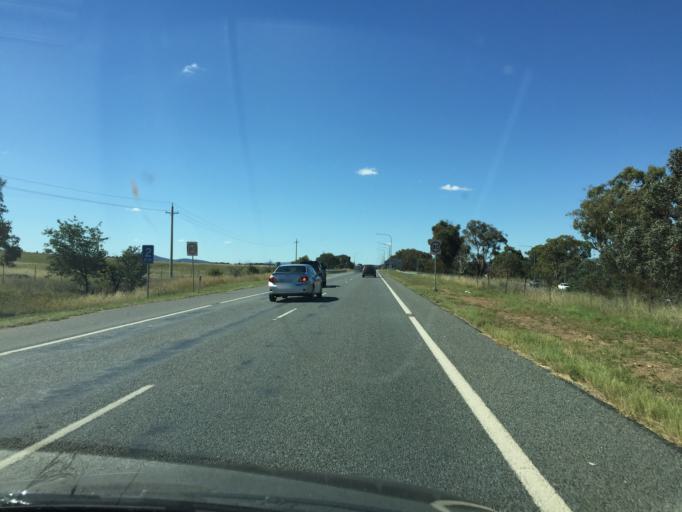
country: AU
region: Australian Capital Territory
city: Macarthur
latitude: -35.3759
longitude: 149.1690
